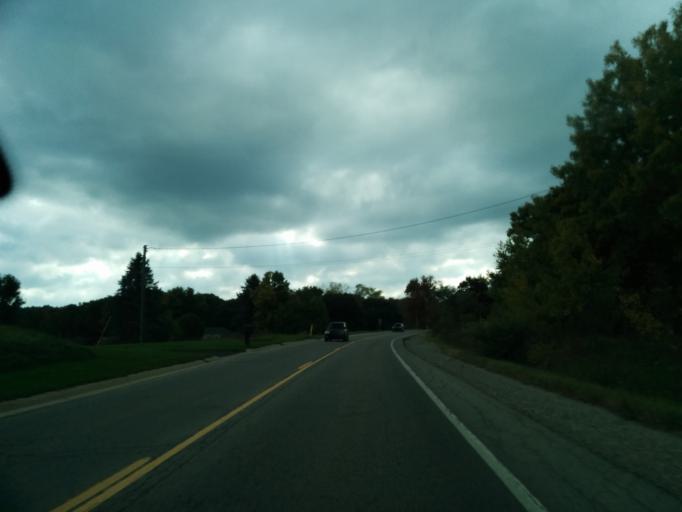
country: US
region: Michigan
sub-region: Oakland County
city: Waterford
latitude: 42.6978
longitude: -83.4634
